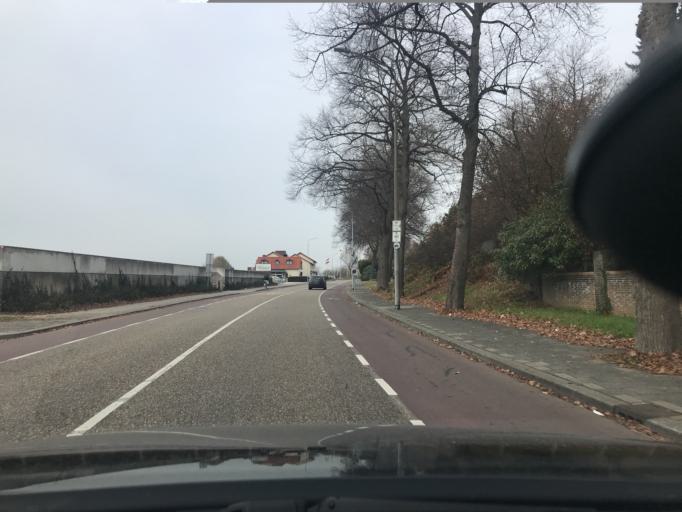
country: NL
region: Limburg
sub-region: Gemeente Venlo
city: Venlo
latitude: 51.3779
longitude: 6.1678
